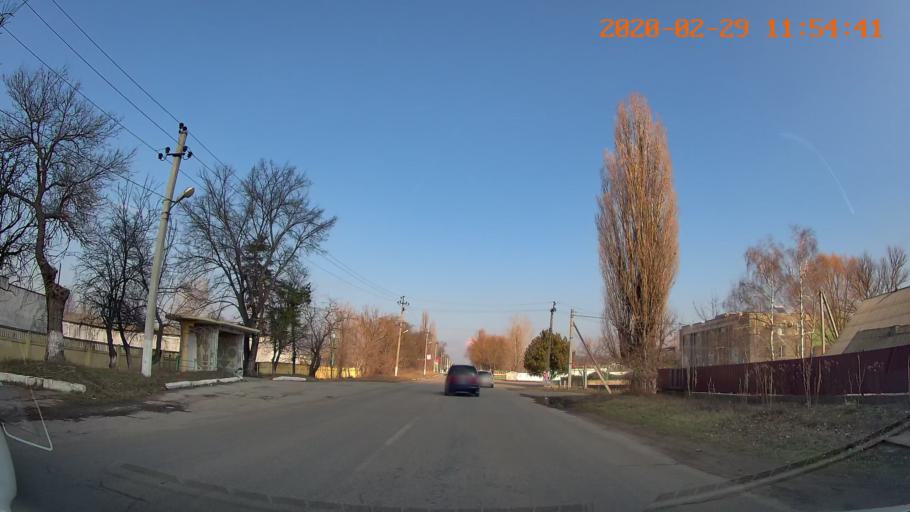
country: MD
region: Telenesti
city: Ribnita
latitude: 47.7857
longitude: 28.9958
